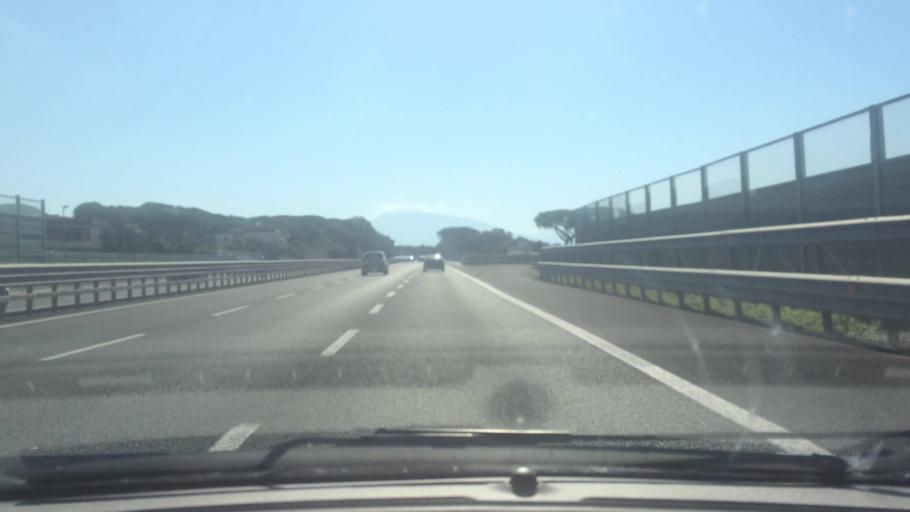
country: IT
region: Campania
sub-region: Provincia di Napoli
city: Ercolano
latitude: 40.8007
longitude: 14.3697
